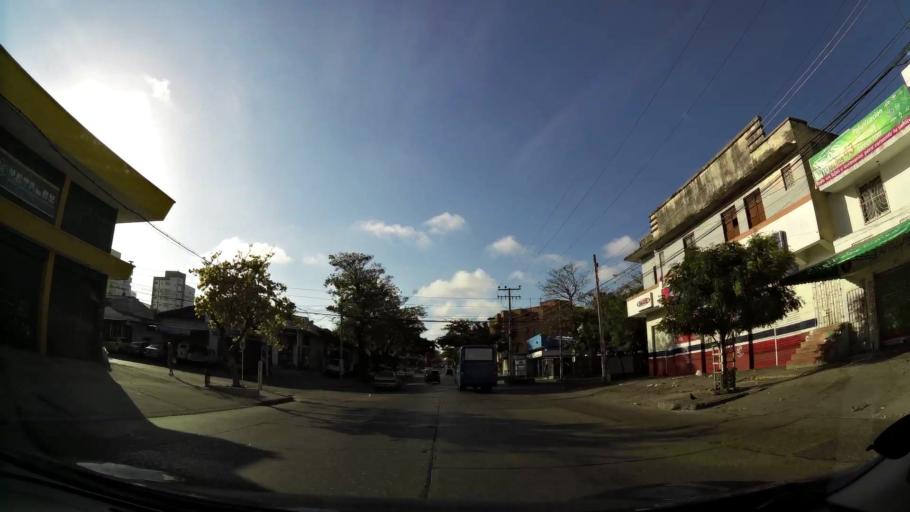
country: CO
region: Atlantico
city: Barranquilla
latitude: 10.9878
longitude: -74.8001
